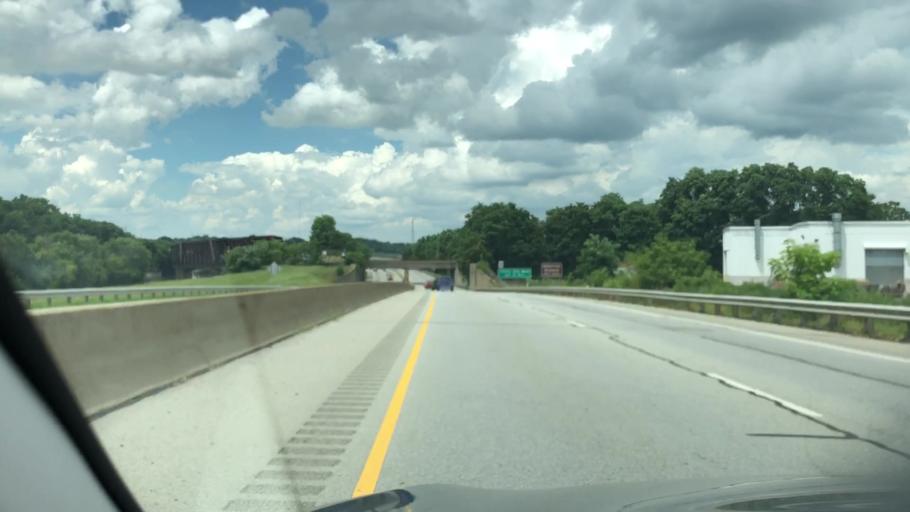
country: US
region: Ohio
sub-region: Stark County
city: Massillon
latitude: 40.7893
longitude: -81.5230
